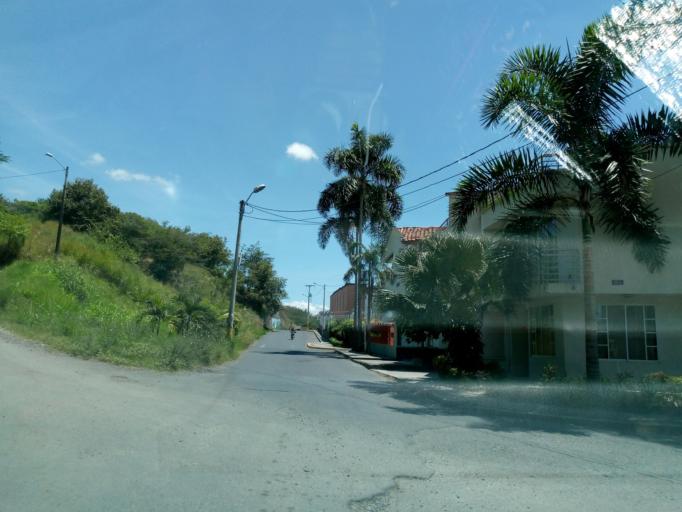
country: CO
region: Valle del Cauca
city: Cartago
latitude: 4.7490
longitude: -75.9254
